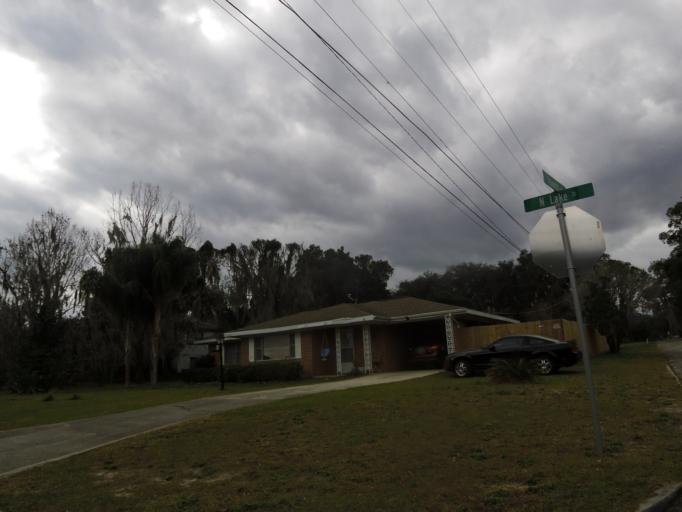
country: US
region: Florida
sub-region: Putnam County
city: Crescent City
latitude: 29.4352
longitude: -81.5072
